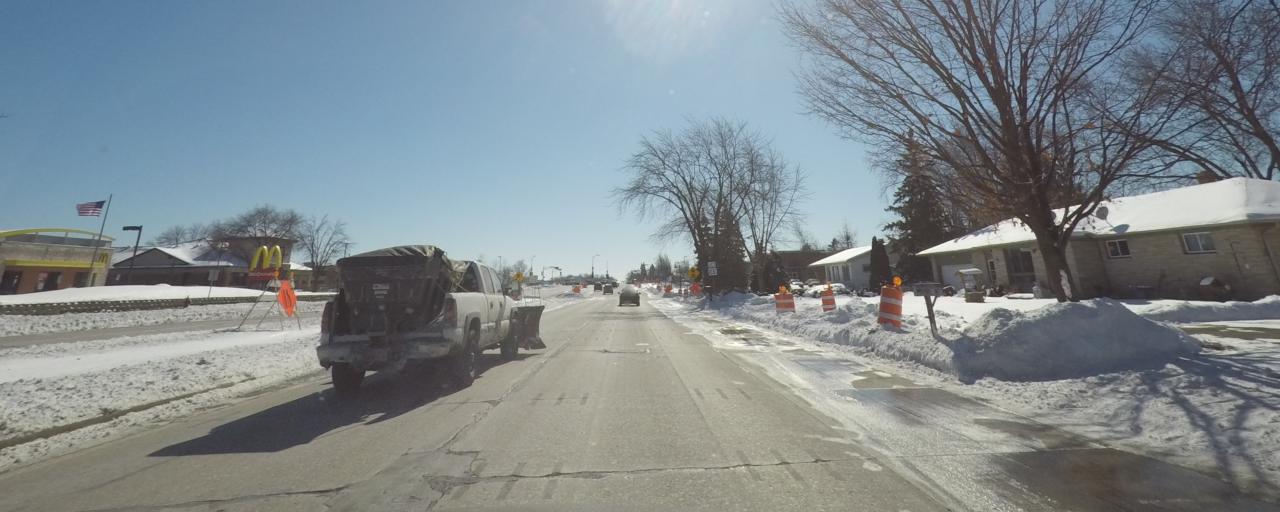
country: US
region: Wisconsin
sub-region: Waukesha County
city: New Berlin
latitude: 42.9785
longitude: -88.1086
